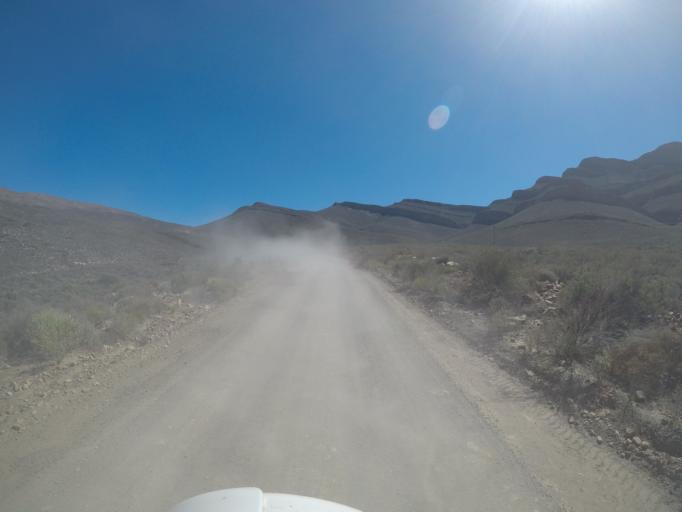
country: ZA
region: Western Cape
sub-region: West Coast District Municipality
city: Clanwilliam
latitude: -32.6244
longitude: 19.3881
